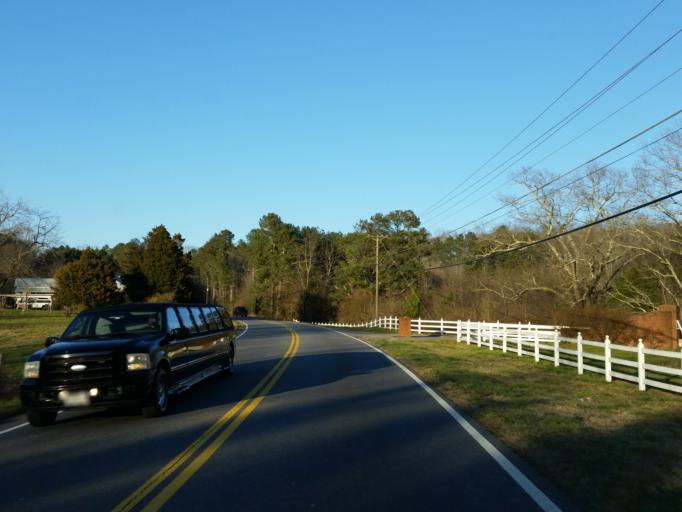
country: US
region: Georgia
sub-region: Cherokee County
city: Holly Springs
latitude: 34.1469
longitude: -84.4442
